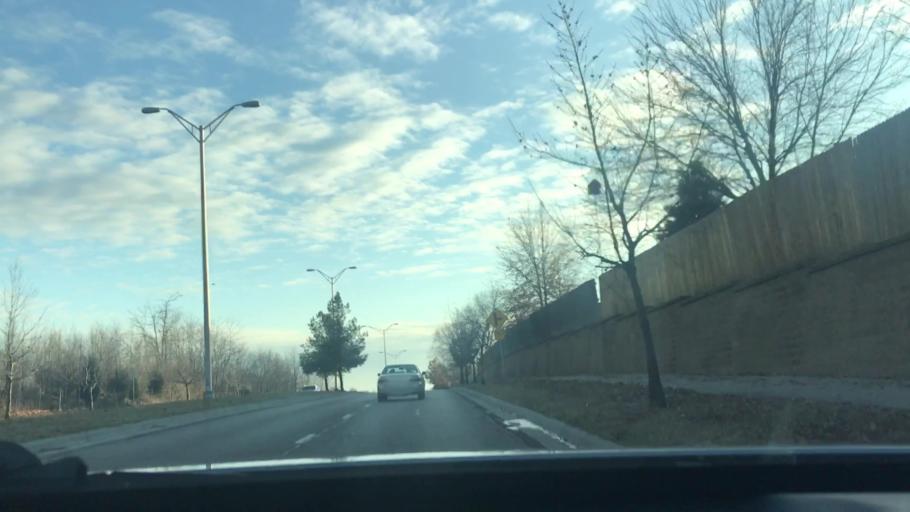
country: US
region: Missouri
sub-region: Jackson County
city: Lees Summit
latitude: 38.9424
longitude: -94.3437
